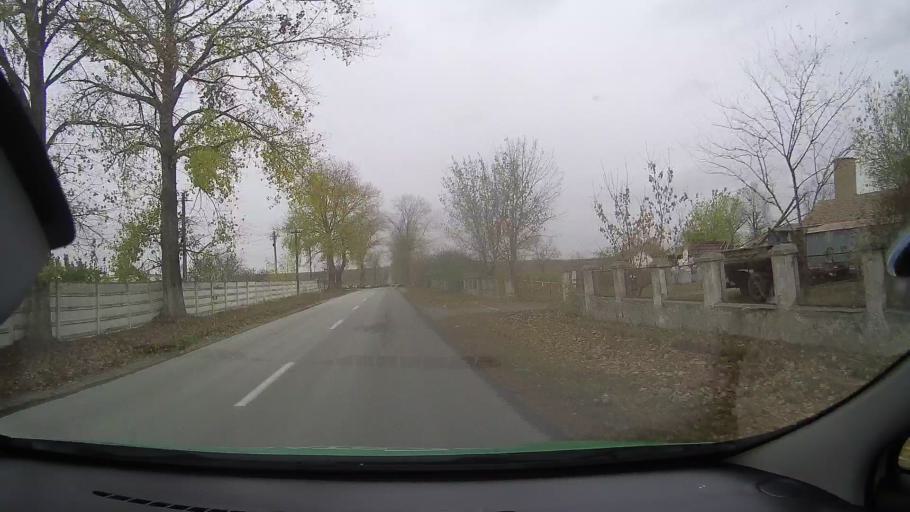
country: RO
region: Constanta
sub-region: Comuna Pantelimon
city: Pantelimon
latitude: 44.5504
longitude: 28.3287
